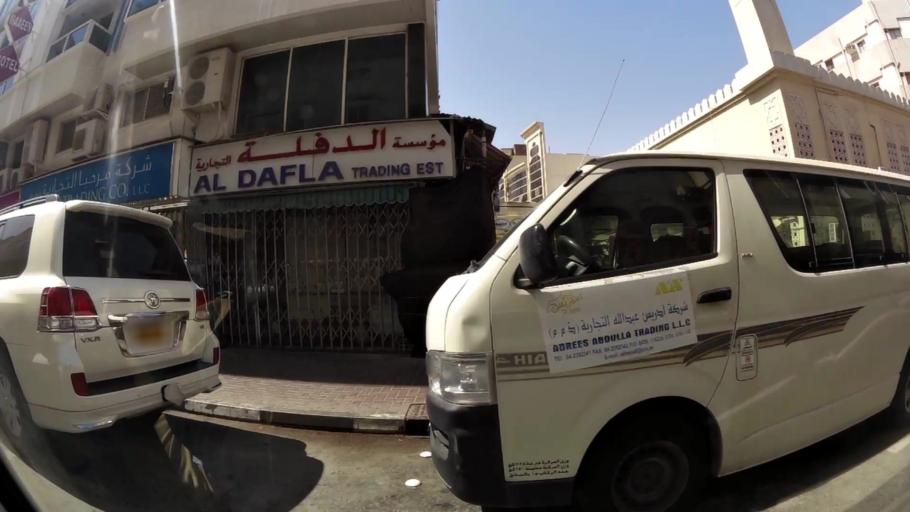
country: AE
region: Ash Shariqah
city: Sharjah
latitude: 25.2693
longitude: 55.3000
